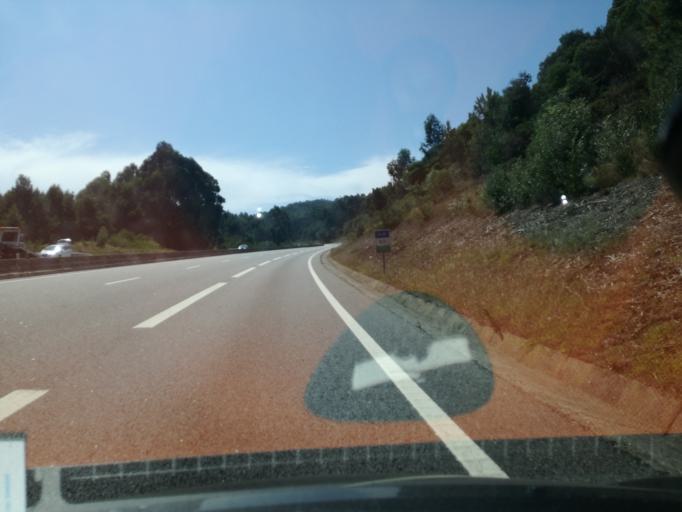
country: PT
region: Viana do Castelo
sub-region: Caminha
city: Vila Praia de Ancora
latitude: 41.7855
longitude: -8.7887
